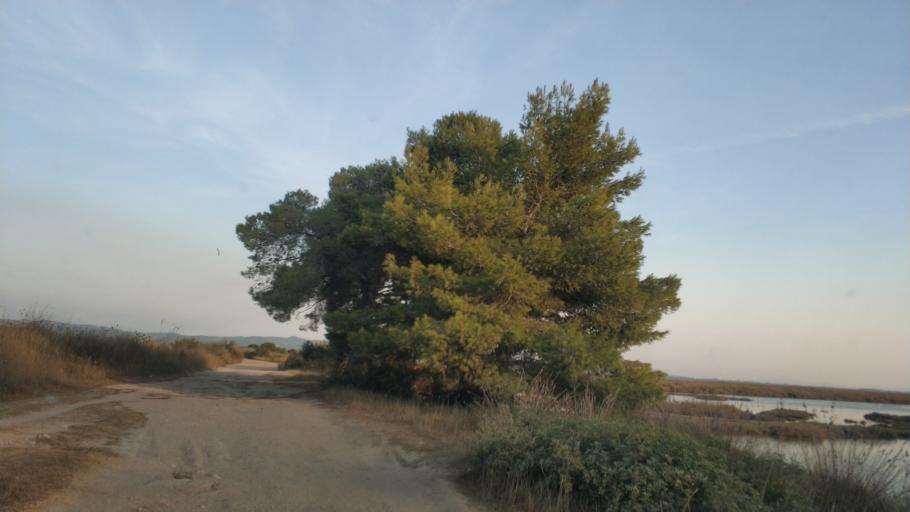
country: AL
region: Fier
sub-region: Rrethi i Lushnjes
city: Divjake
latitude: 40.9514
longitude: 19.4765
